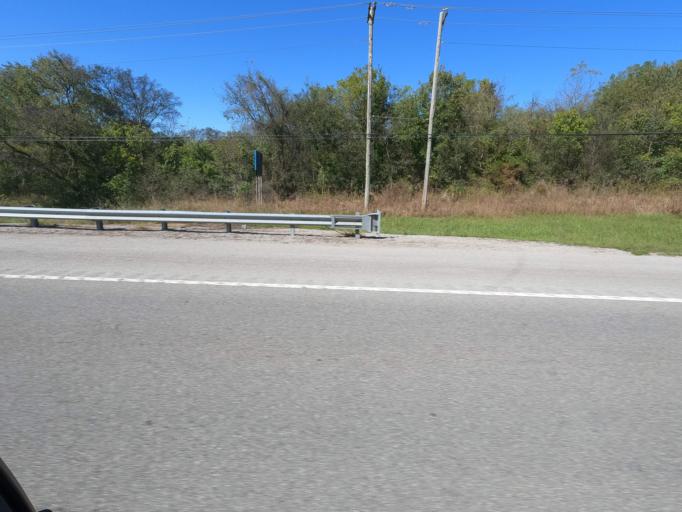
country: US
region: Tennessee
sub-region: Maury County
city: Mount Pleasant
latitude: 35.5050
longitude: -87.2305
